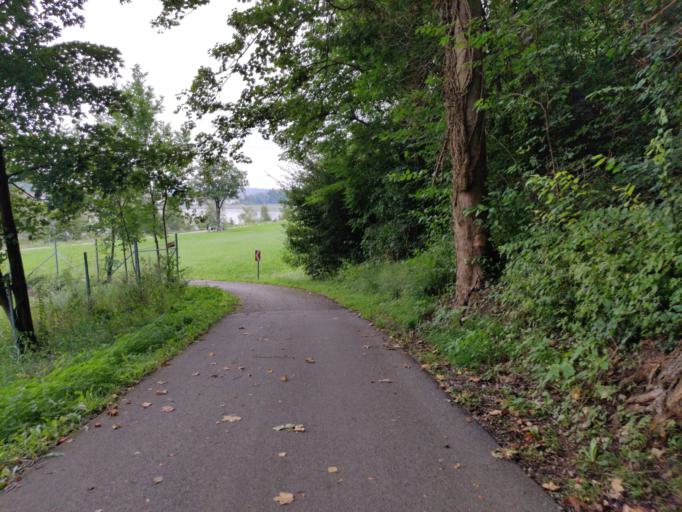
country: AT
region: Lower Austria
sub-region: Politischer Bezirk Melk
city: Ybbs an der Donau
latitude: 48.1867
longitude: 15.0701
